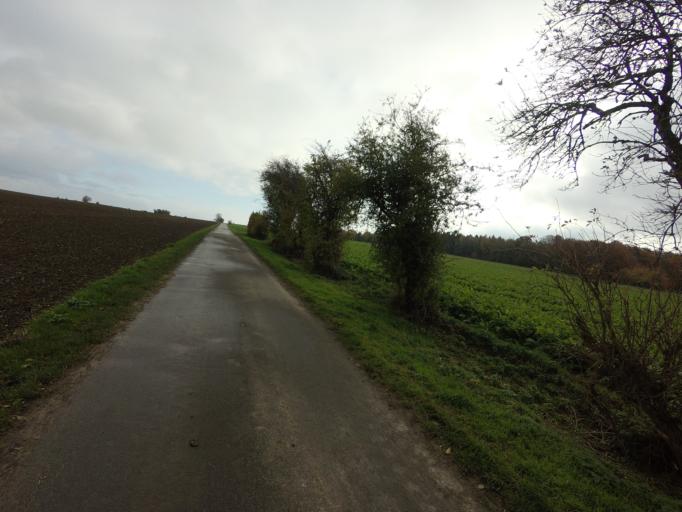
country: NL
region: Limburg
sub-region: Gemeente Vaals
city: Vaals
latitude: 50.7897
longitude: 6.0168
